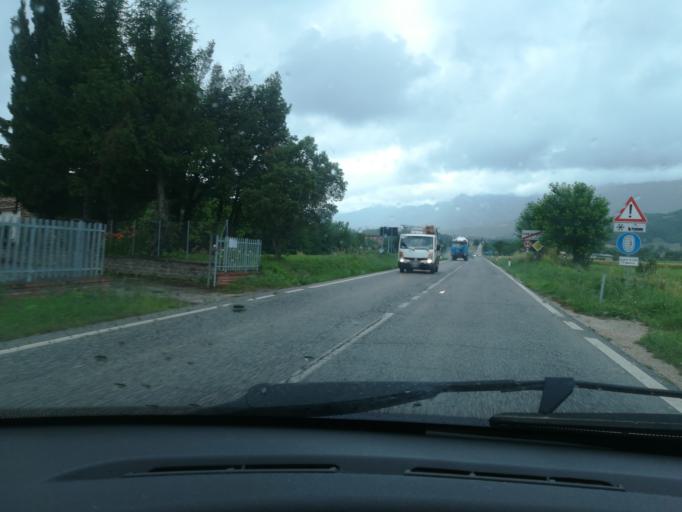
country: IT
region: The Marches
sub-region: Provincia di Macerata
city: Cessapalombo
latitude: 43.0755
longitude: 13.2793
